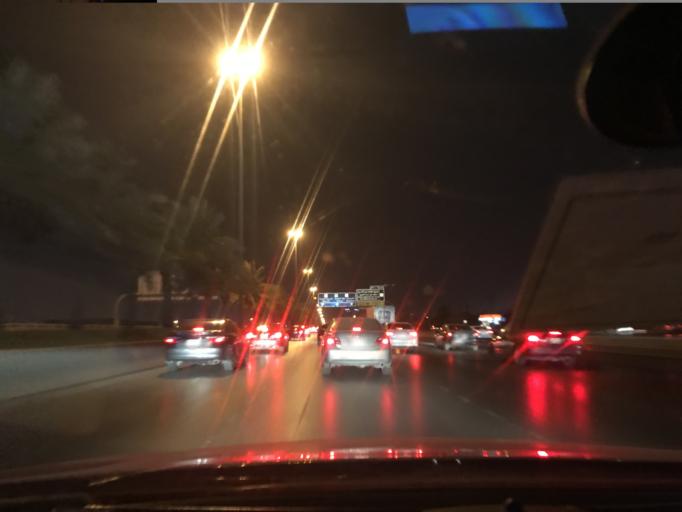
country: SA
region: Ar Riyad
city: Riyadh
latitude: 24.7668
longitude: 46.7354
